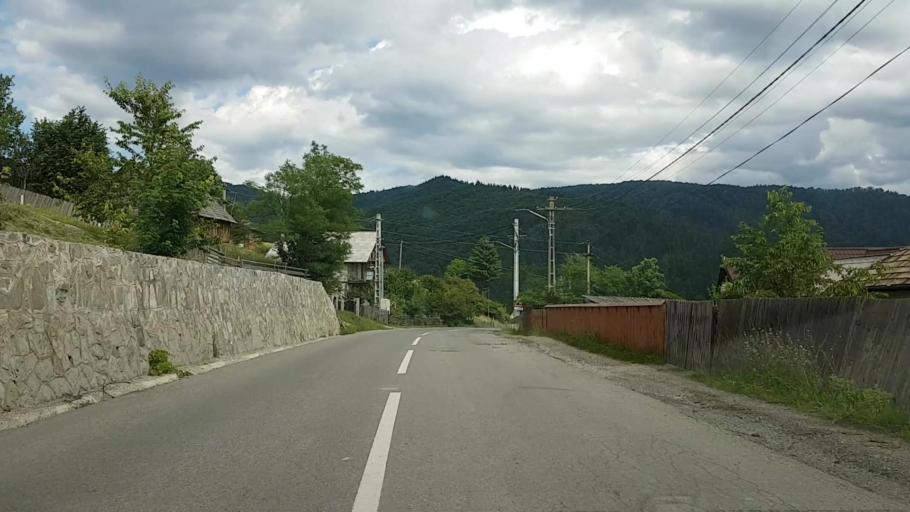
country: RO
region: Neamt
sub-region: Comuna Bicaz
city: Dodeni
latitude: 46.9865
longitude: 26.1039
